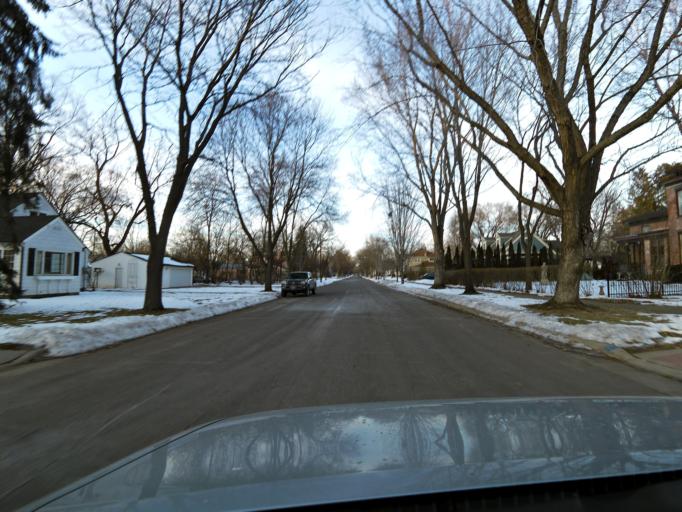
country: US
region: Wisconsin
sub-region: Saint Croix County
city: Hudson
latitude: 44.9791
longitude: -92.7479
